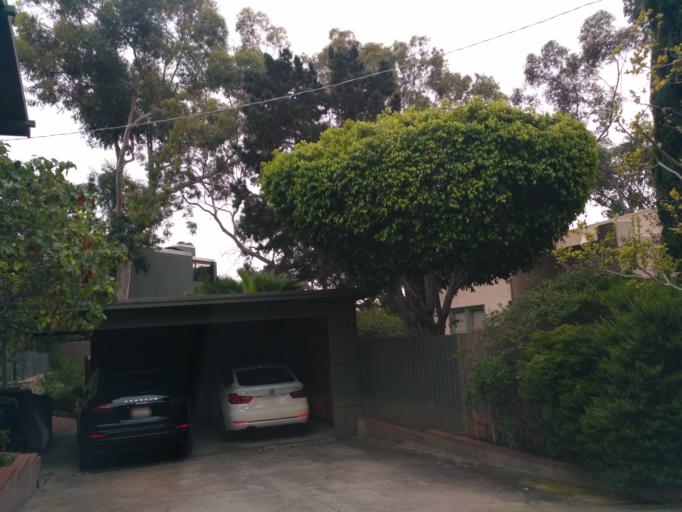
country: US
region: California
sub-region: San Diego County
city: San Diego
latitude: 32.7387
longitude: -117.1653
